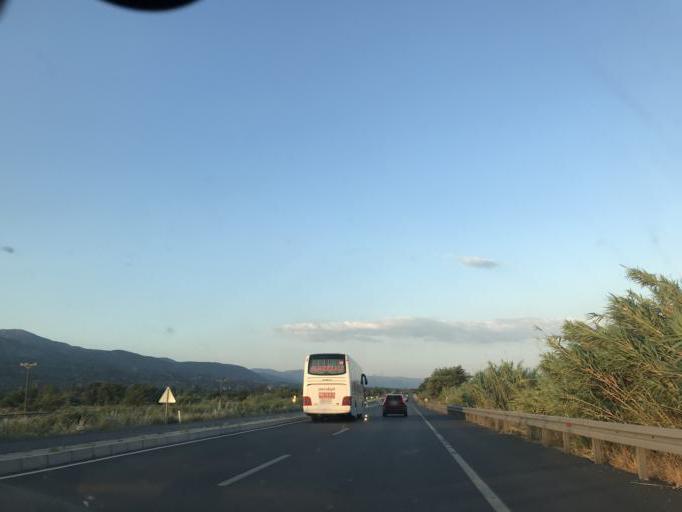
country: TR
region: Aydin
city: Pamukoren
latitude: 37.9105
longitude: 28.5646
